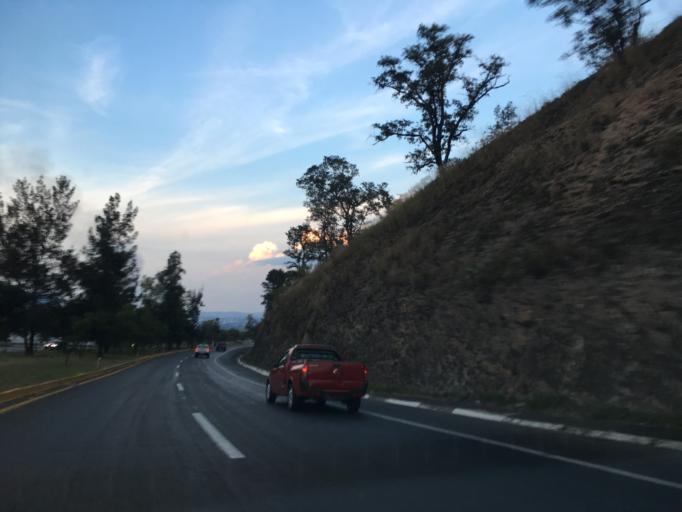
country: MX
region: Michoacan
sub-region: Morelia
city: La Mintzita (Piedra Dura)
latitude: 19.6342
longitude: -101.2722
